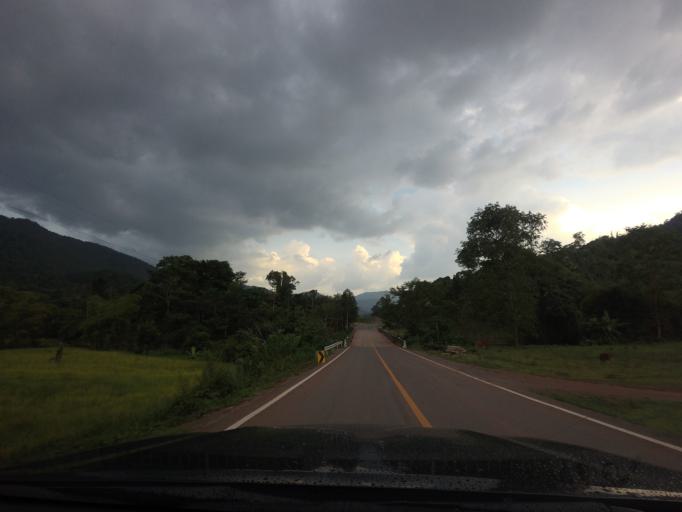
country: TH
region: Nan
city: Bo Kluea
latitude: 19.2309
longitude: 101.1825
